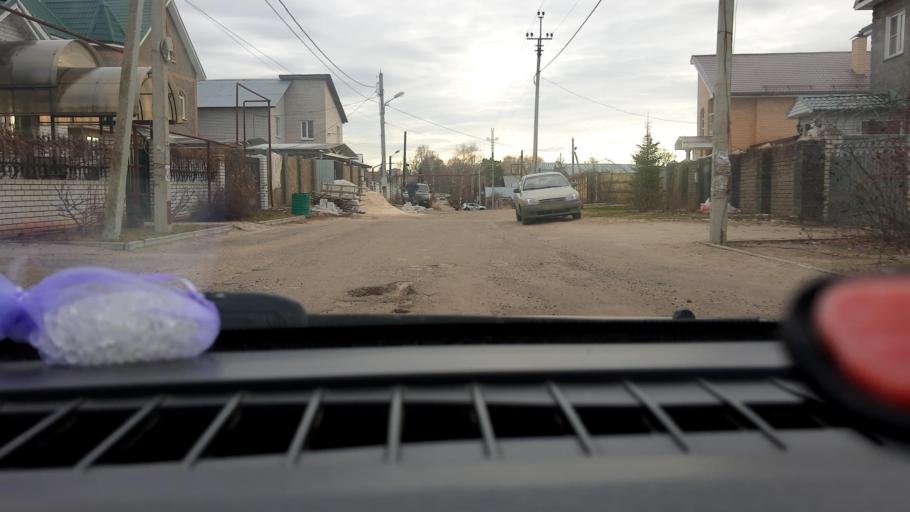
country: RU
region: Nizjnij Novgorod
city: Gorbatovka
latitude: 56.3844
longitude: 43.7738
